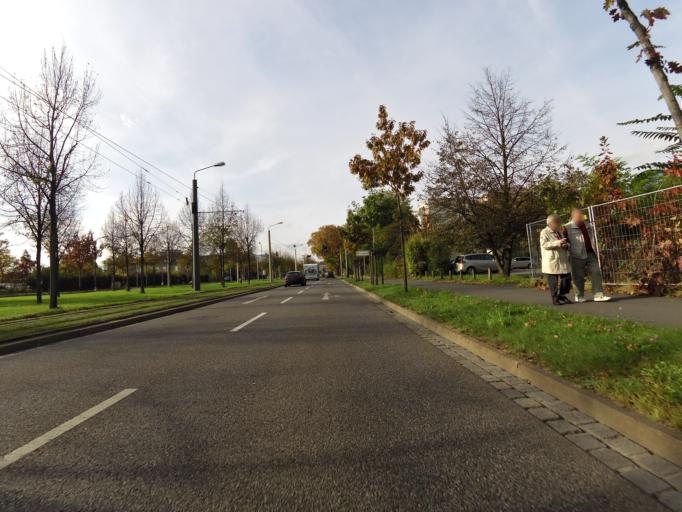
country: DE
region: Saxony
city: Dresden
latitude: 51.0437
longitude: 13.7618
